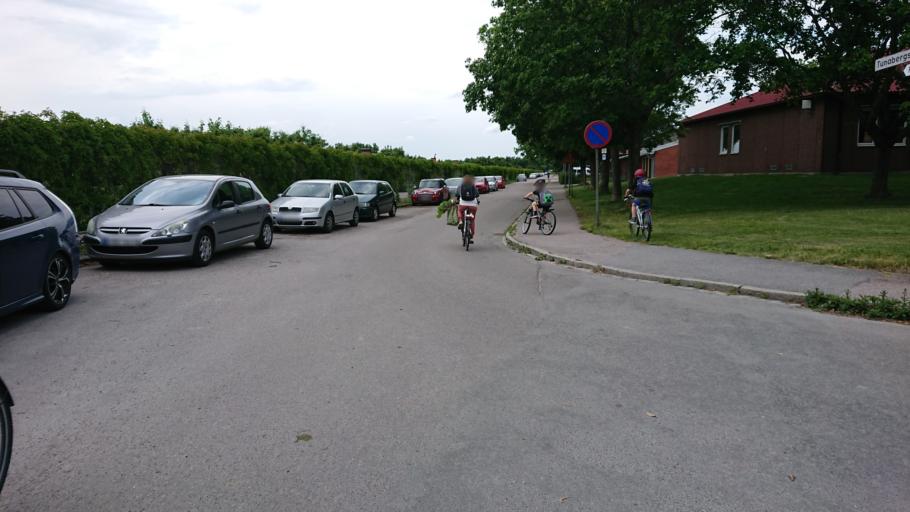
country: SE
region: Uppsala
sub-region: Uppsala Kommun
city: Uppsala
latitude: 59.8744
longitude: 17.6162
